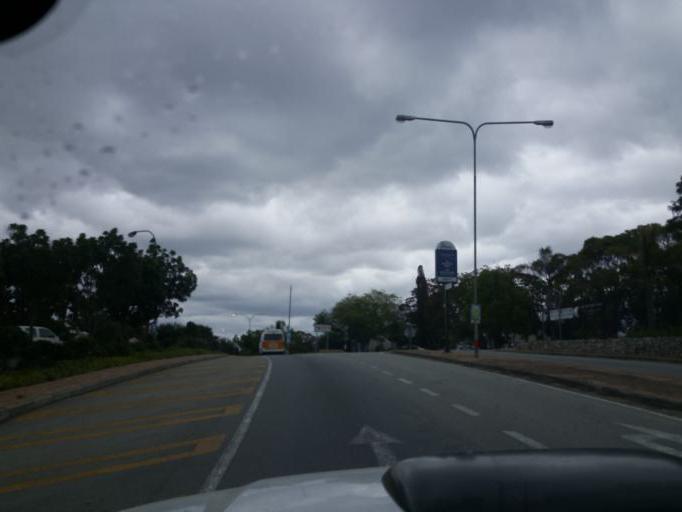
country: ZA
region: Western Cape
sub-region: Eden District Municipality
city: George
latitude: -33.9516
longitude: 22.4517
